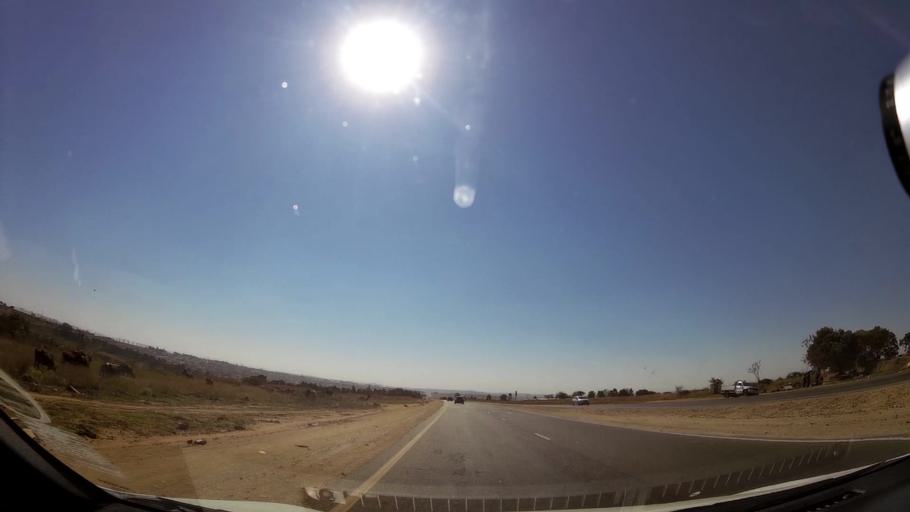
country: ZA
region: Gauteng
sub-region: City of Johannesburg Metropolitan Municipality
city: Midrand
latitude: -25.9370
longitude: 28.0959
